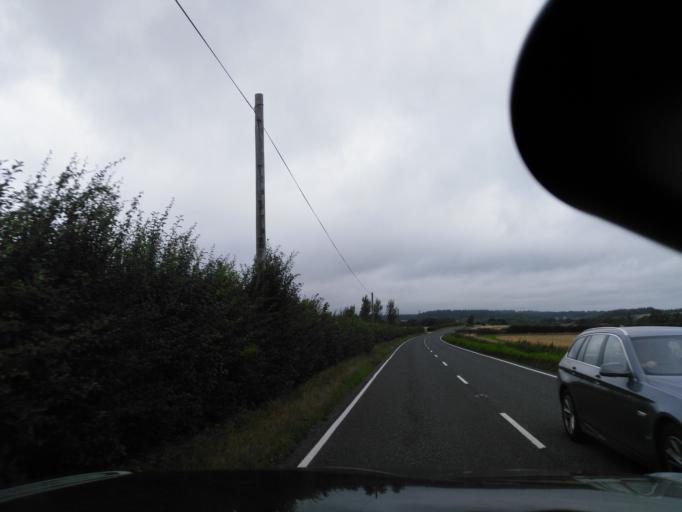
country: GB
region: England
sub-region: Wiltshire
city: Bishopstrow
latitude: 51.1577
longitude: -2.1758
